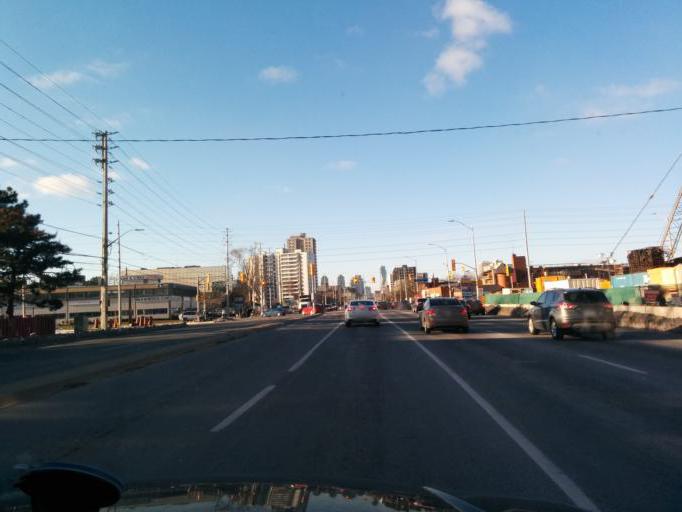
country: CA
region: Ontario
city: Mississauga
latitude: 43.5735
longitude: -79.6067
